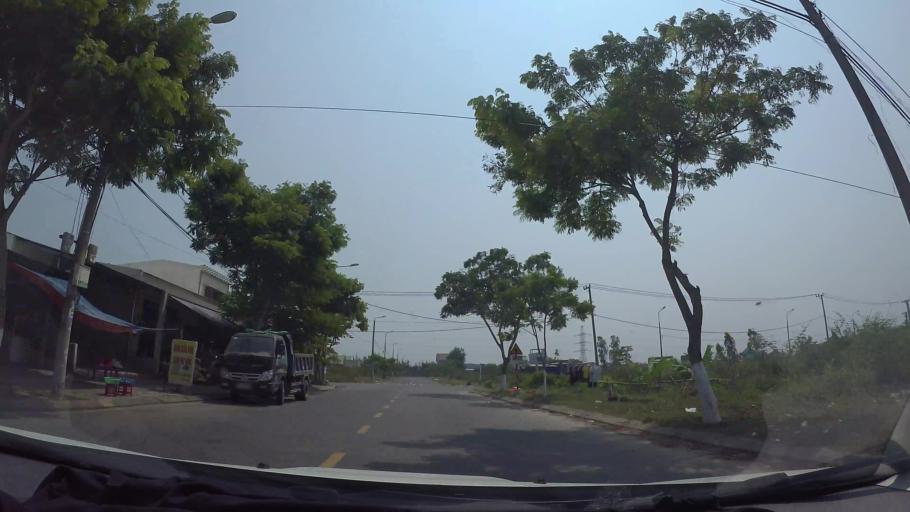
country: VN
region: Da Nang
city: Cam Le
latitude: 15.9959
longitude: 108.1968
